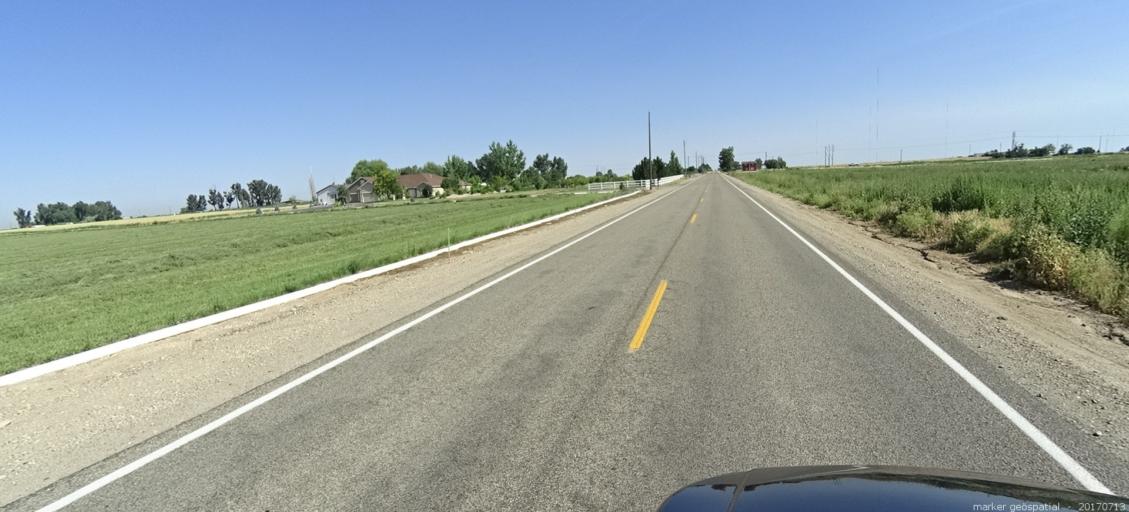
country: US
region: Idaho
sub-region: Ada County
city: Kuna
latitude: 43.5428
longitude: -116.4138
